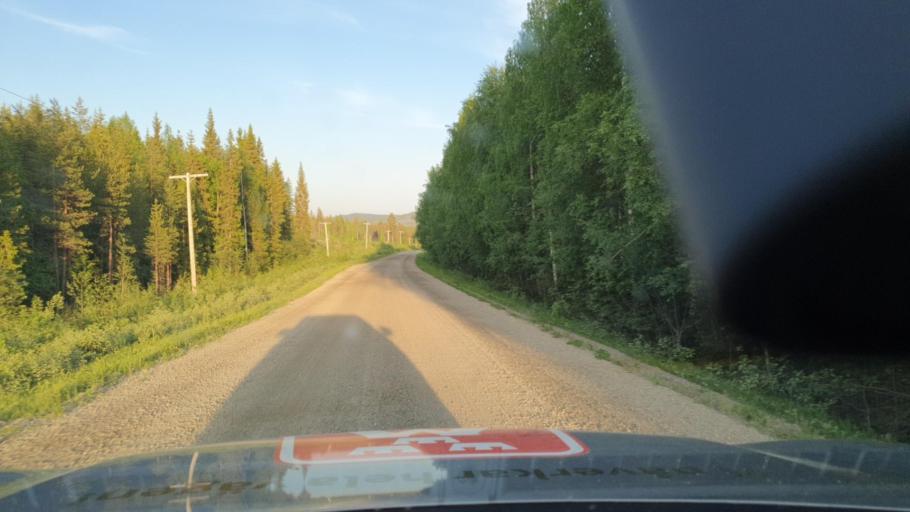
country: SE
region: Norrbotten
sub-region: Bodens Kommun
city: Boden
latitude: 66.1691
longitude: 21.5322
